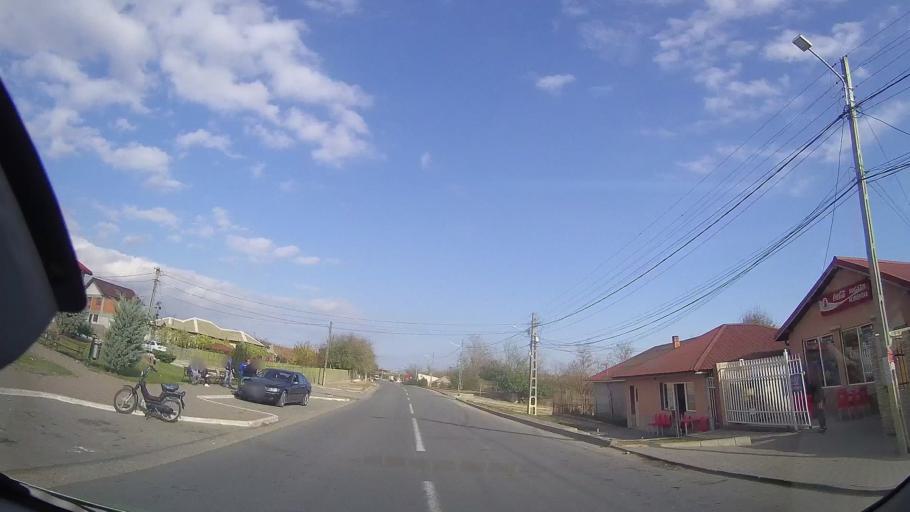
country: RO
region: Constanta
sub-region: Comuna Douazeci si Trei August
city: Dulcesti
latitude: 43.9055
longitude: 28.5458
